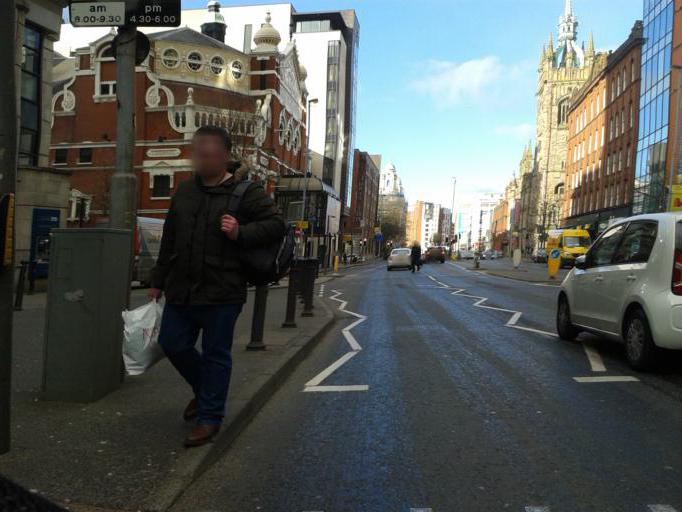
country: GB
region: Northern Ireland
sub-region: City of Belfast
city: Belfast
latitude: 54.5948
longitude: -5.9345
